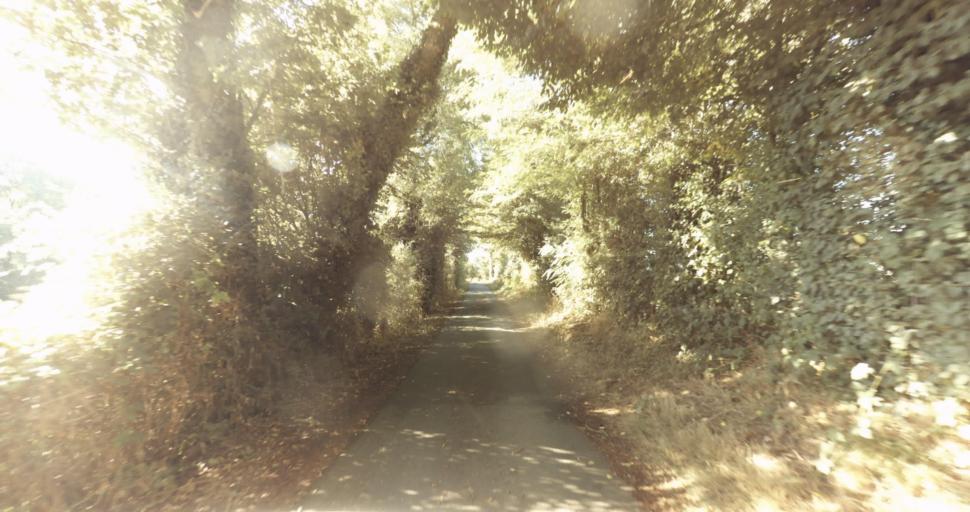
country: FR
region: Lower Normandy
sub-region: Departement de l'Orne
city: Vimoutiers
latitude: 48.8957
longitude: 0.1324
